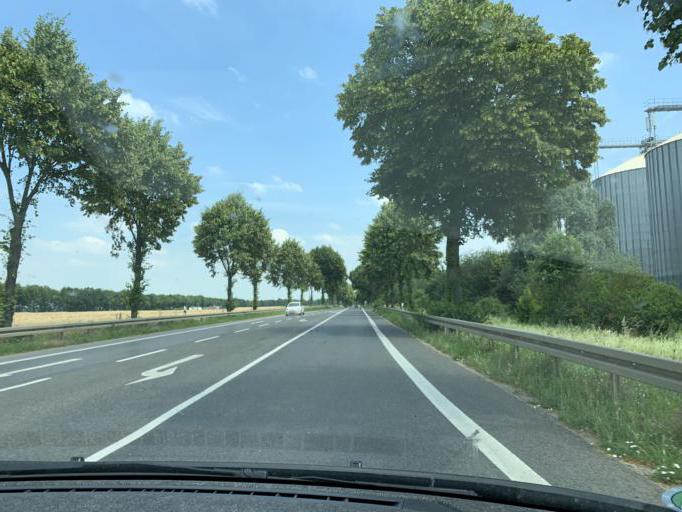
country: DE
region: North Rhine-Westphalia
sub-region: Regierungsbezirk Koln
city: Aldenhoven
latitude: 50.9049
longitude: 6.3093
